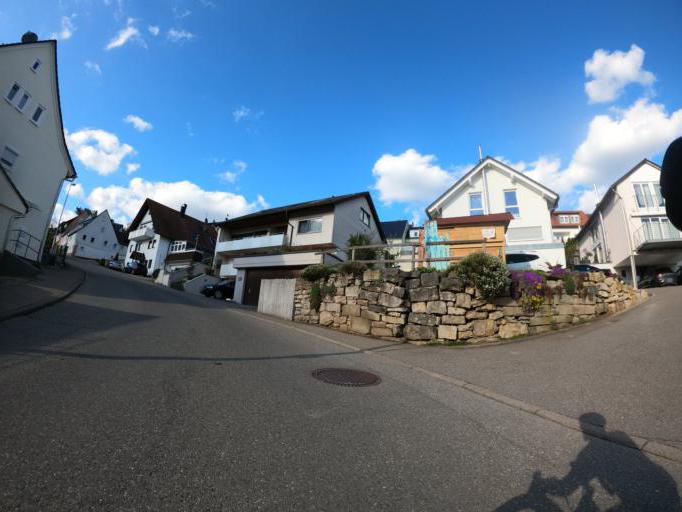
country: DE
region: Baden-Wuerttemberg
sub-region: Regierungsbezirk Stuttgart
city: Aidlingen
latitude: 48.6819
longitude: 8.8676
